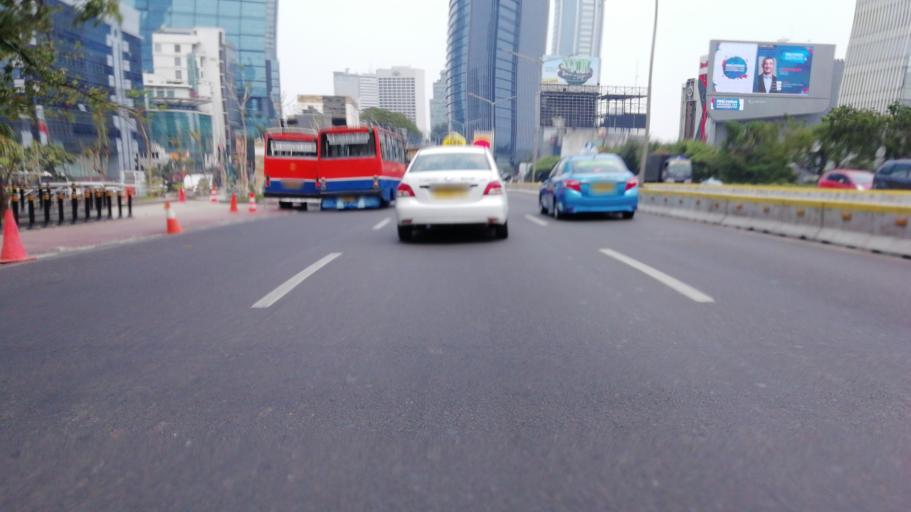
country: ID
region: Jakarta Raya
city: Jakarta
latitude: -6.2019
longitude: 106.8229
